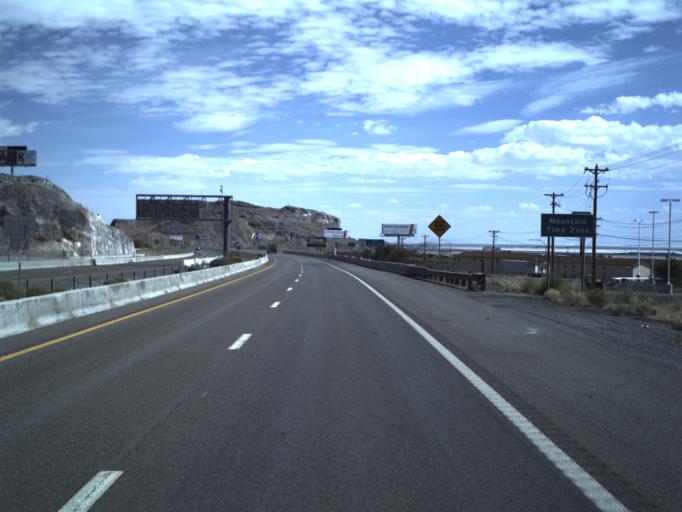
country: US
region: Utah
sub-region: Tooele County
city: Wendover
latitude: 40.7379
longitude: -114.0450
